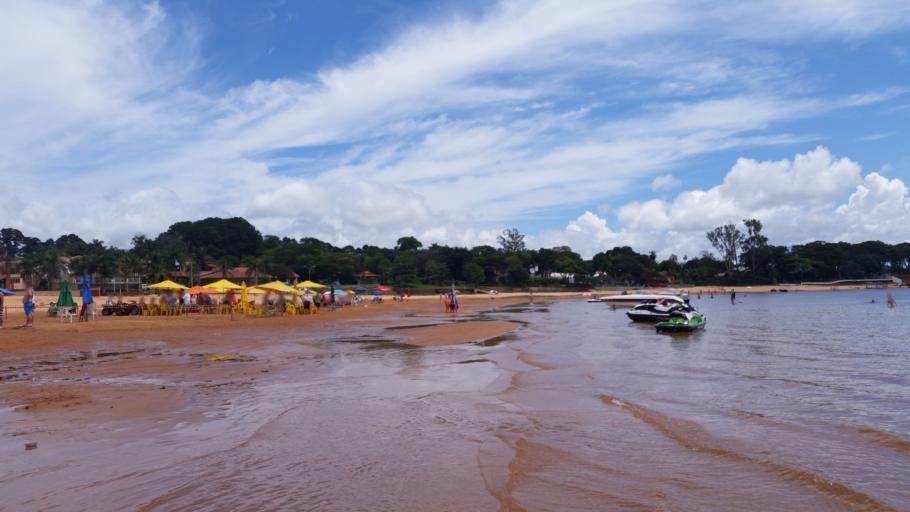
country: BR
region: Sao Paulo
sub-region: Itai
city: Itai
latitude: -23.2803
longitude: -49.0194
